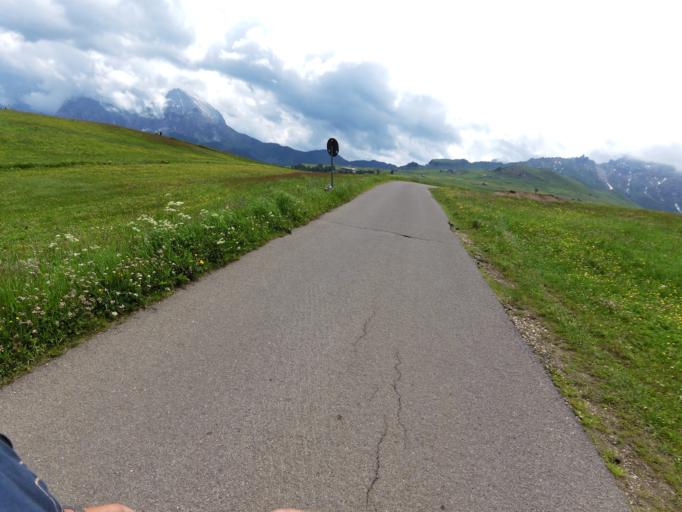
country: IT
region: Trentino-Alto Adige
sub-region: Bolzano
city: Ortisei
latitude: 46.5327
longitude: 11.6292
